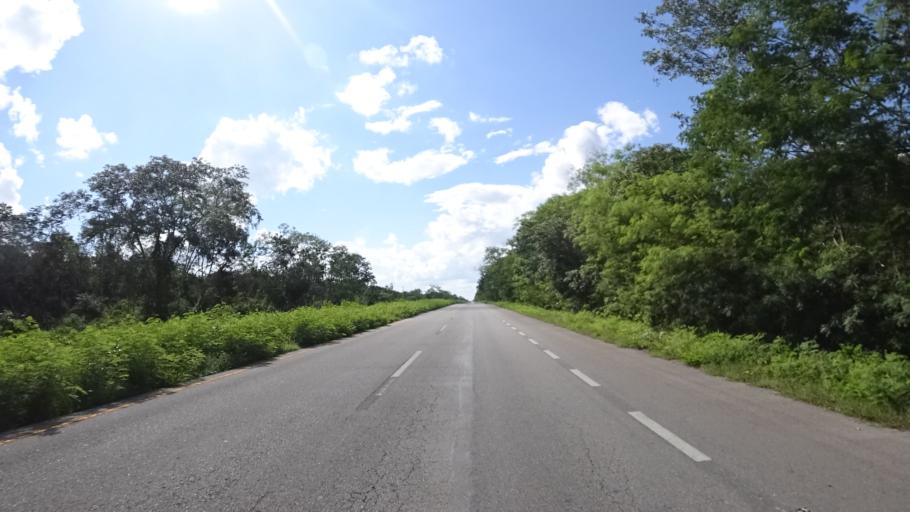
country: MX
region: Yucatan
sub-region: Hocaba
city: Sahcaba
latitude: 20.8170
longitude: -89.1122
